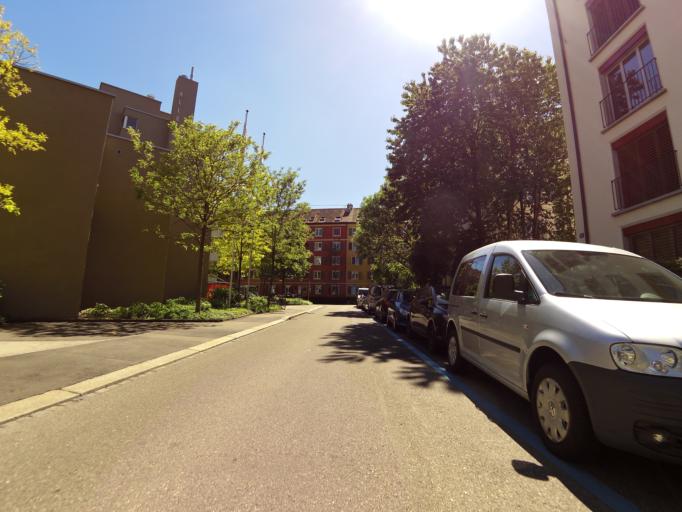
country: CH
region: Zurich
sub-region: Bezirk Zuerich
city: Zuerich (Kreis 3) / Sihlfeld
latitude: 47.3711
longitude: 8.5115
